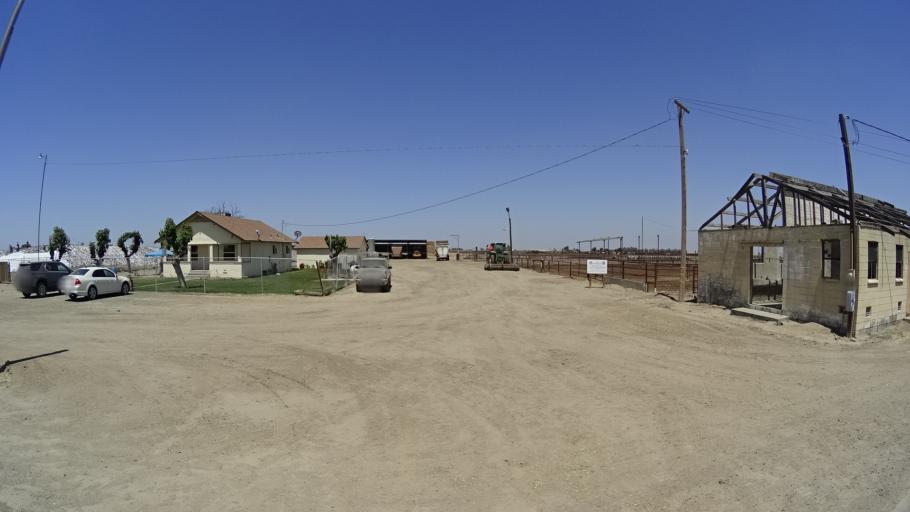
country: US
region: California
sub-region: Kings County
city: Home Garden
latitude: 36.1969
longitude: -119.6337
